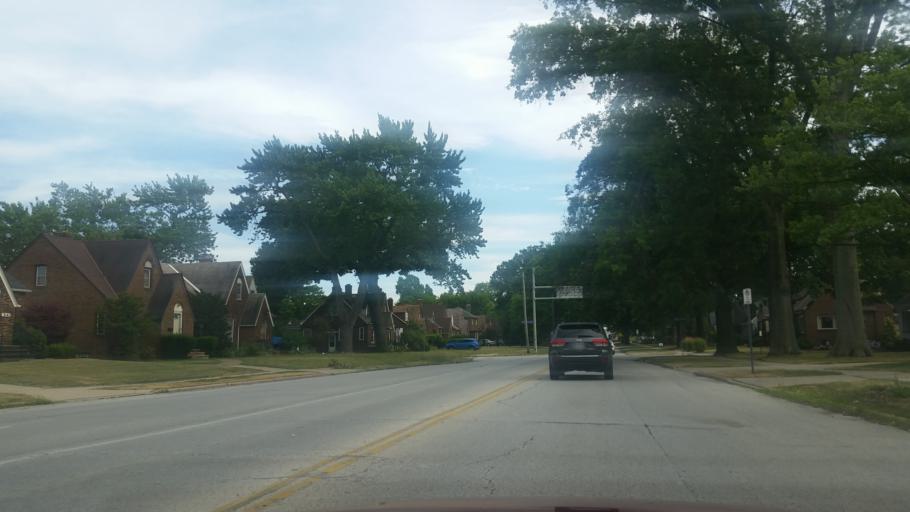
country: US
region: Ohio
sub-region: Cuyahoga County
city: Lakewood
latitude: 41.4680
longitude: -81.7899
